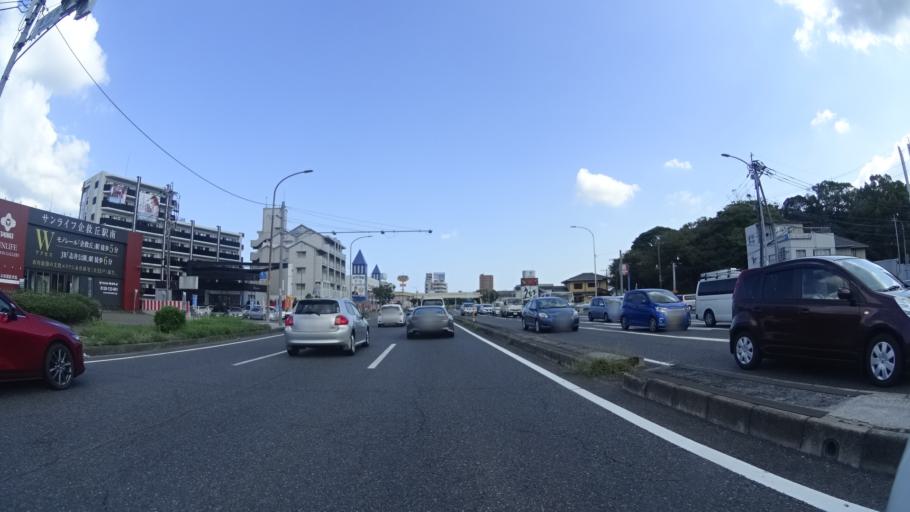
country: JP
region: Fukuoka
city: Kanda
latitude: 33.8306
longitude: 130.9239
